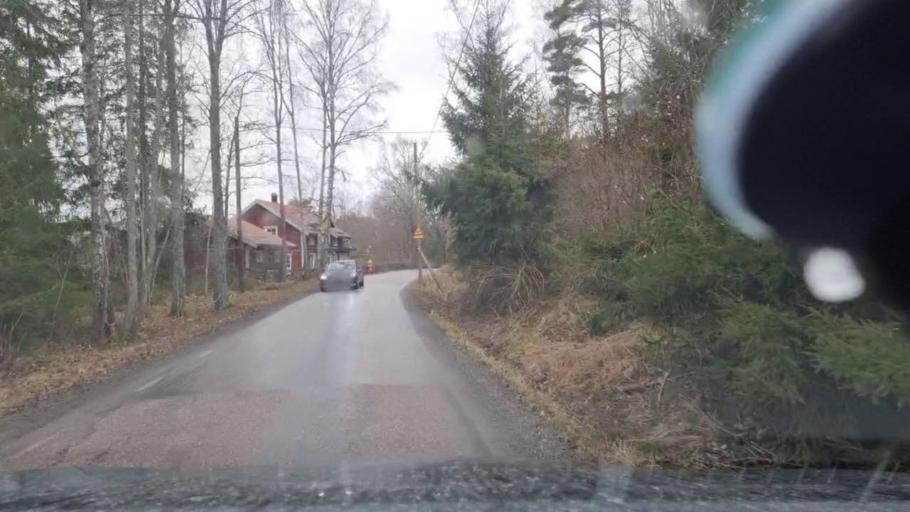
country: SE
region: Stockholm
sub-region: Taby Kommun
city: Taby
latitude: 59.4797
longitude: 18.0189
